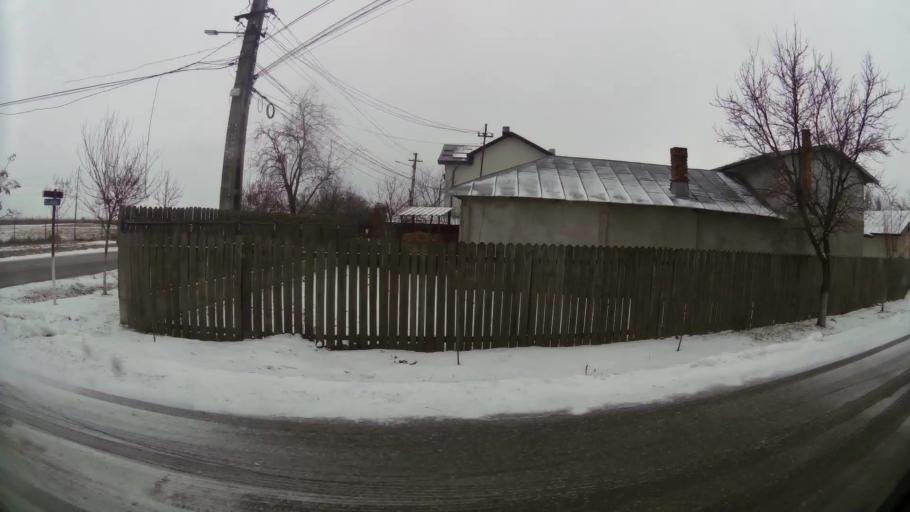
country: RO
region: Prahova
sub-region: Comuna Berceni
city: Corlatesti
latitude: 44.9243
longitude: 26.0727
